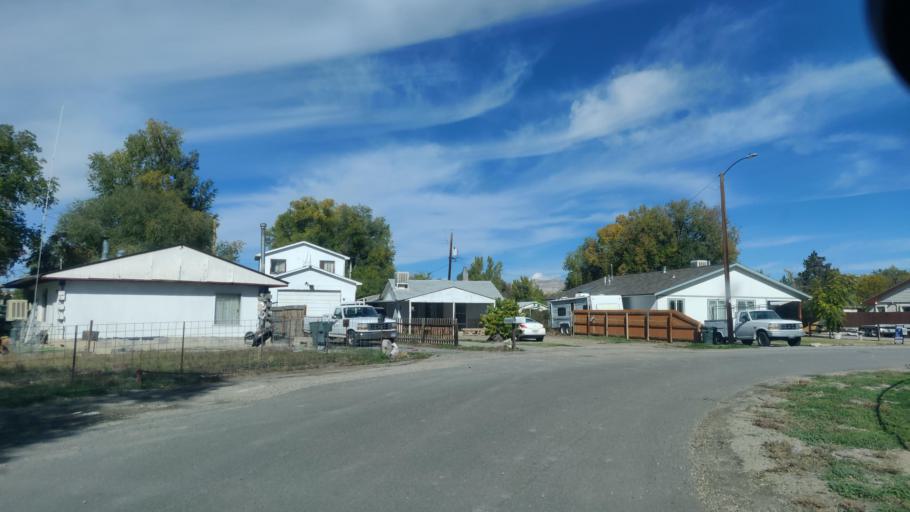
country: US
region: Colorado
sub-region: Mesa County
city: Fruitvale
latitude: 39.0803
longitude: -108.5169
